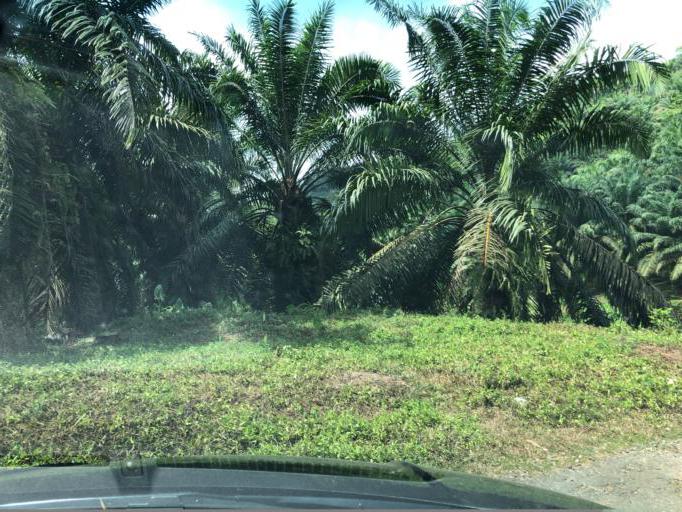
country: LK
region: Western
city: Horawala Junction
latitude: 6.5489
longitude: 80.0930
